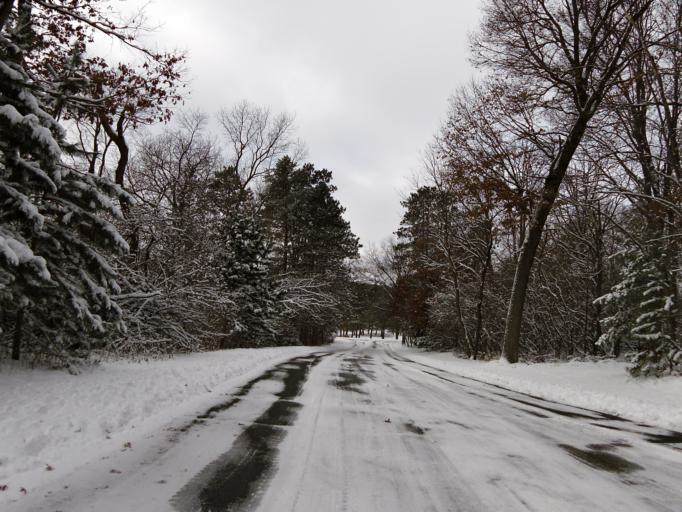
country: US
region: Minnesota
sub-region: Washington County
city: Lake Elmo
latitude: 44.9727
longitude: -92.8281
